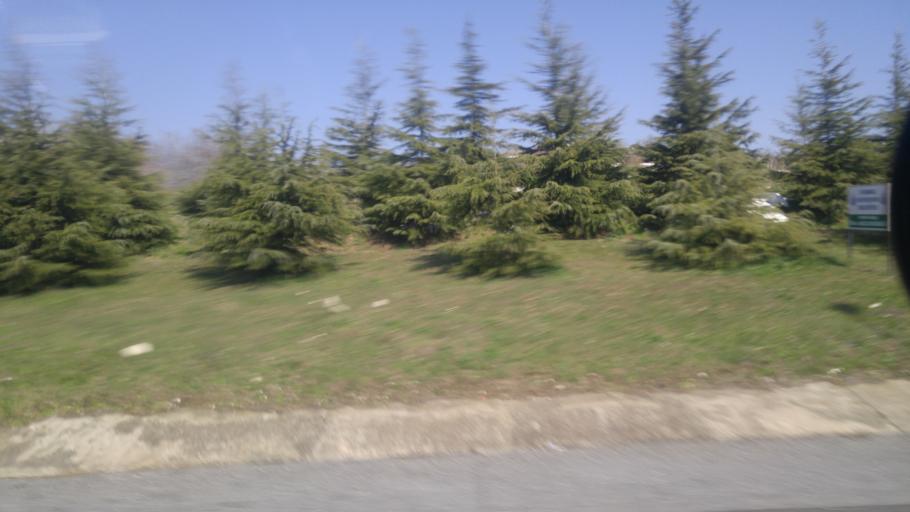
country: TR
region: Istanbul
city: Celaliye
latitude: 41.0599
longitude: 28.4114
